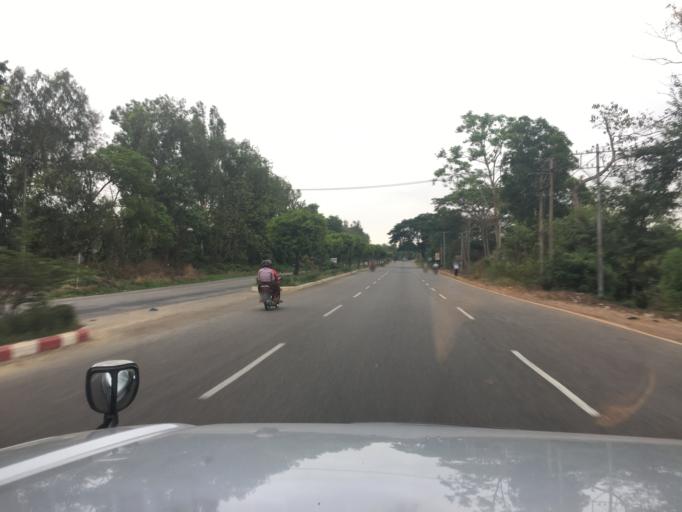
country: MM
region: Bago
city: Bago
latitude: 17.2176
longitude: 96.4314
